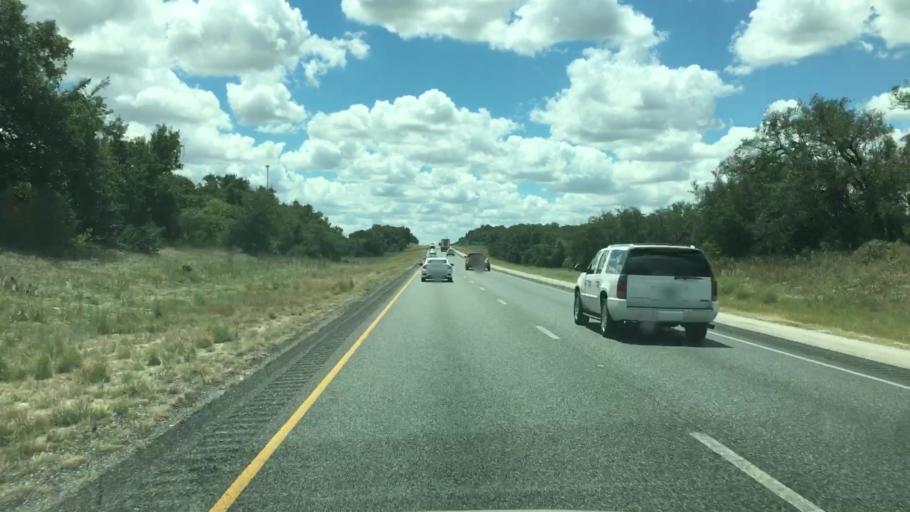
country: US
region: Texas
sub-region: Bexar County
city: Elmendorf
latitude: 29.1947
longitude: -98.4220
